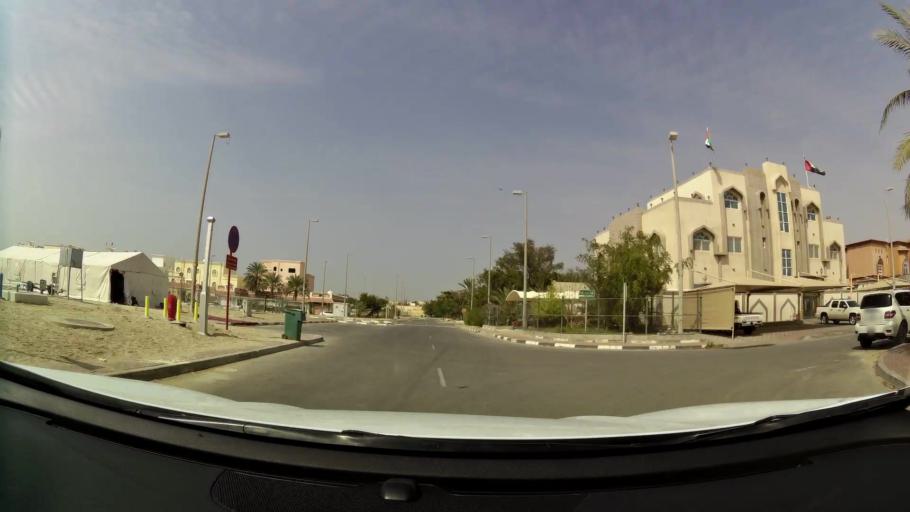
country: AE
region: Abu Dhabi
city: Abu Dhabi
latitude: 24.5466
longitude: 54.6815
